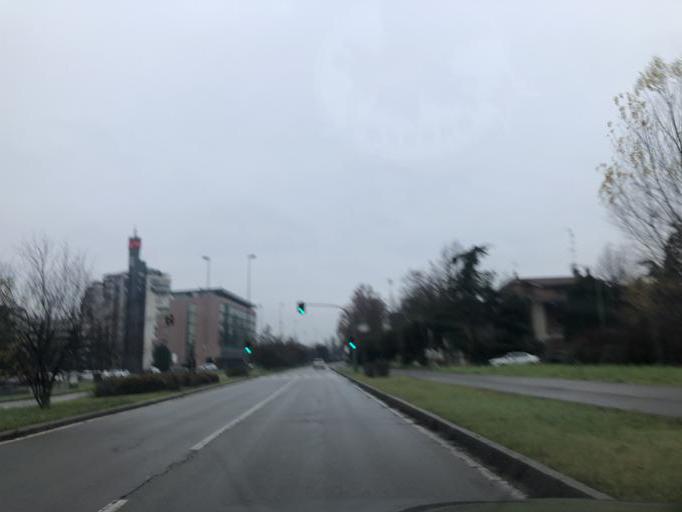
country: IT
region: Emilia-Romagna
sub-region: Provincia di Modena
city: Modena
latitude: 44.6387
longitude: 10.9002
